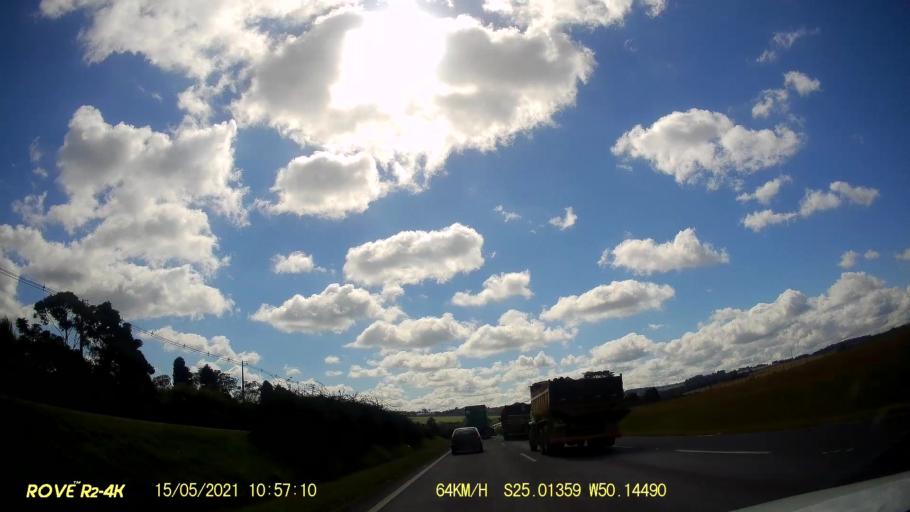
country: BR
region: Parana
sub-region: Carambei
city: Carambei
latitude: -25.0134
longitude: -50.1449
